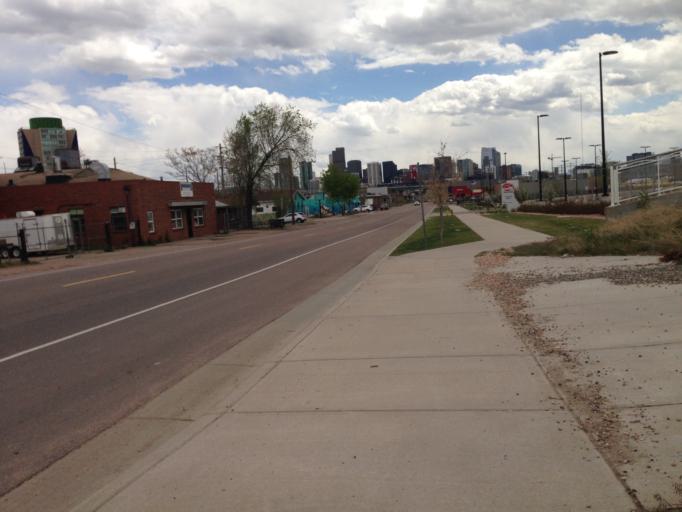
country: US
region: Colorado
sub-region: Denver County
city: Denver
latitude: 39.7738
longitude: -104.9949
